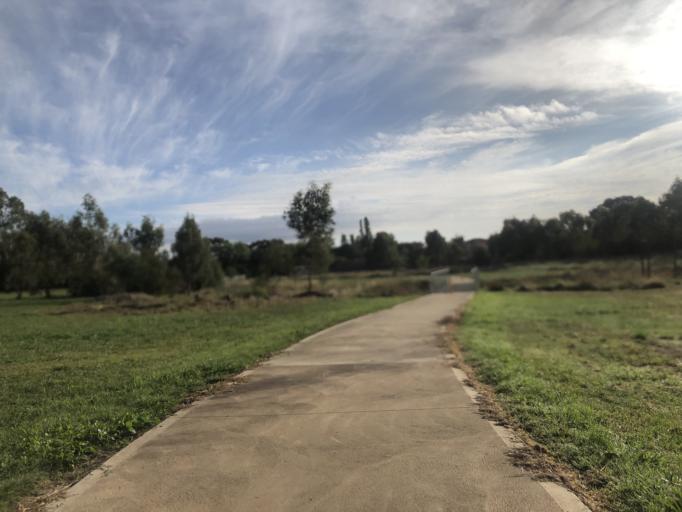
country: AU
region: New South Wales
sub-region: Orange Municipality
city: Orange
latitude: -33.2953
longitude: 149.0920
